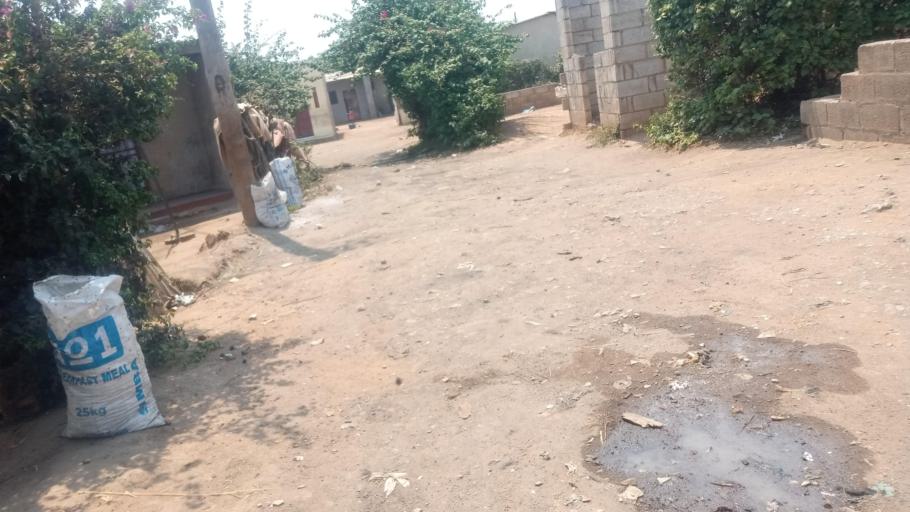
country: ZM
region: Lusaka
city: Lusaka
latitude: -15.4452
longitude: 28.3823
